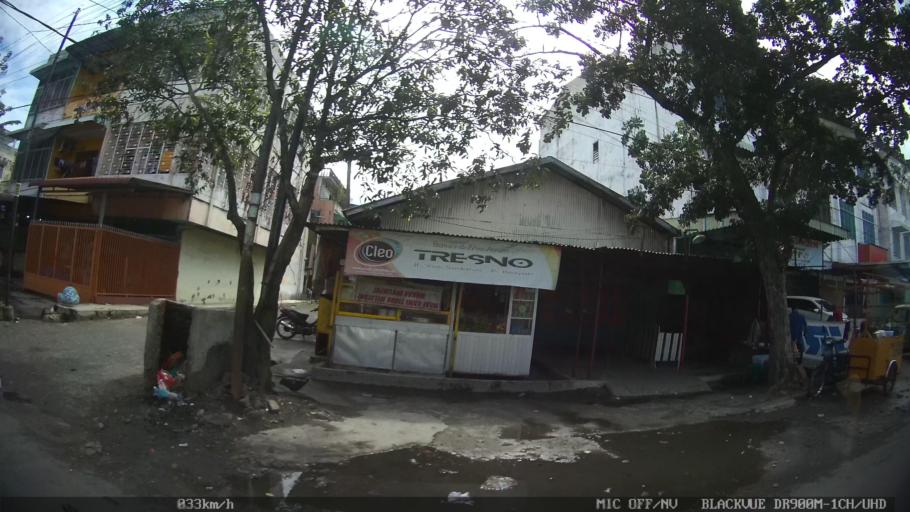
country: ID
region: North Sumatra
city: Medan
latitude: 3.6246
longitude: 98.6692
